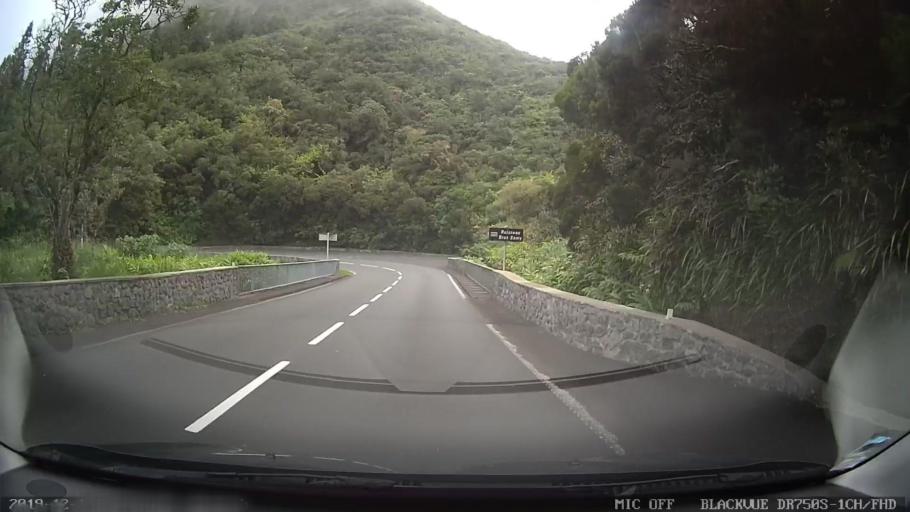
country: RE
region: Reunion
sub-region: Reunion
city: Cilaos
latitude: -21.1566
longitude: 55.6022
